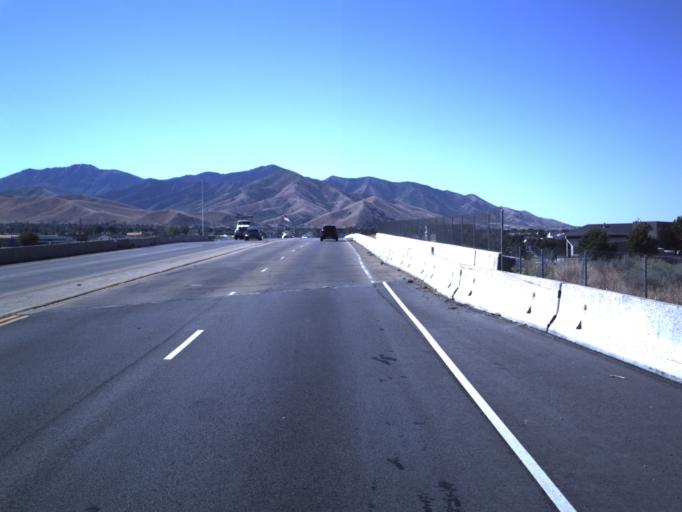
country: US
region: Utah
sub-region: Tooele County
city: Tooele
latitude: 40.5627
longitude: -112.2964
